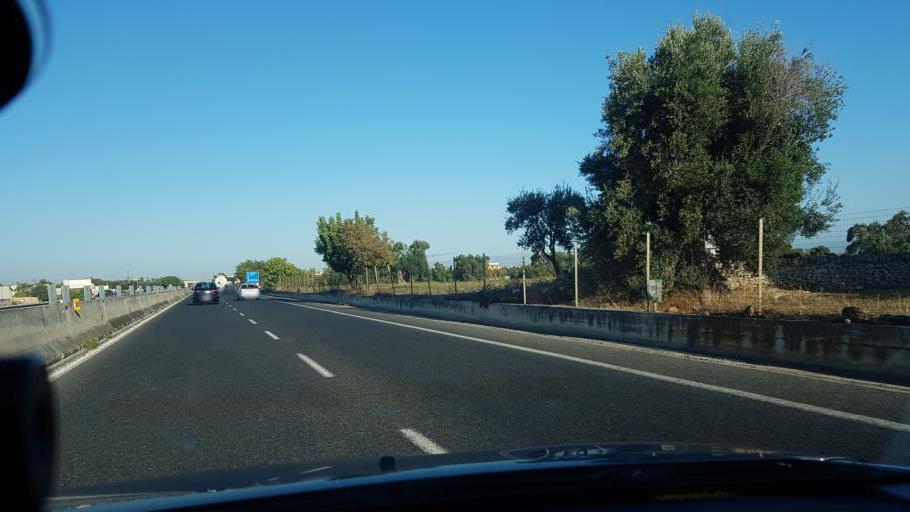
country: IT
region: Apulia
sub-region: Provincia di Bari
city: Monopoli
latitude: 40.9323
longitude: 17.2988
